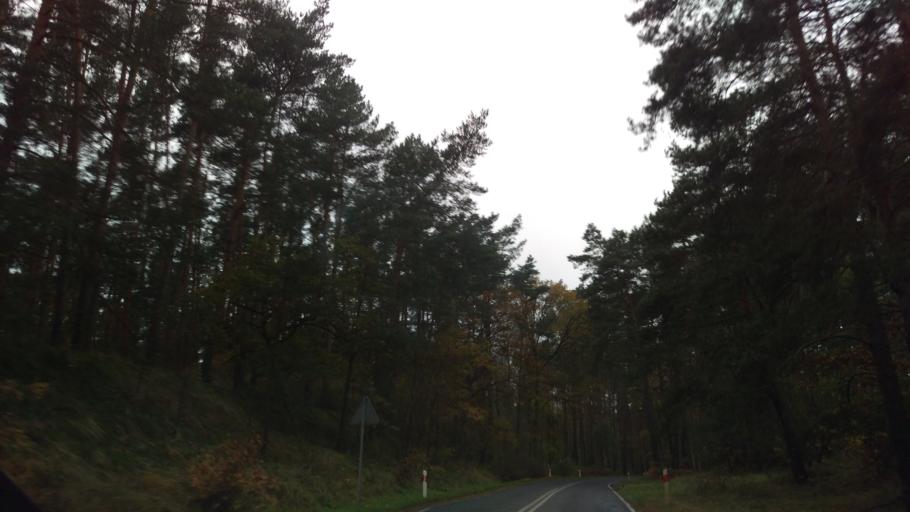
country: PL
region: West Pomeranian Voivodeship
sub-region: Powiat gryfinski
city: Stare Czarnowo
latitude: 53.3936
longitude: 14.7439
